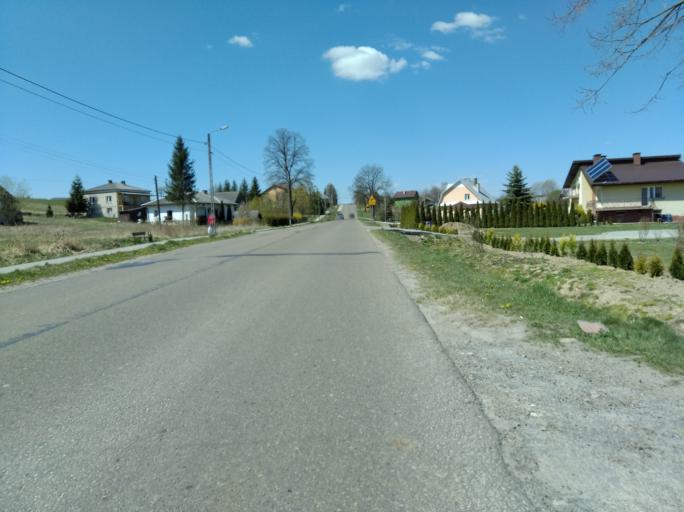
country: PL
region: Subcarpathian Voivodeship
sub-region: Powiat brzozowski
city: Dydnia
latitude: 49.6894
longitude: 22.1627
